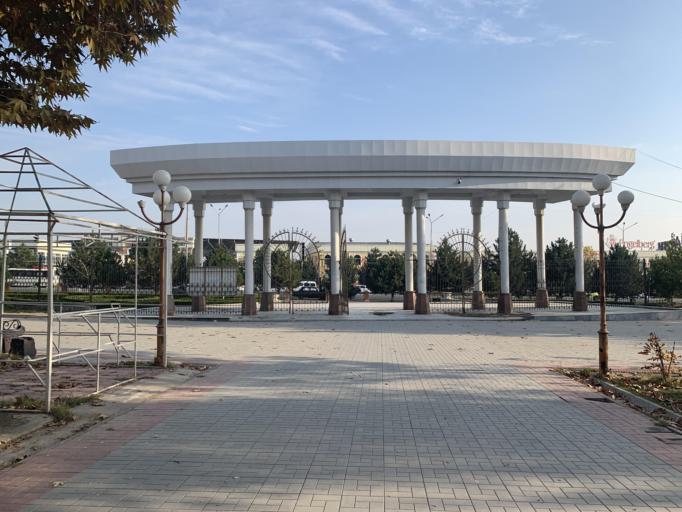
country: UZ
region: Namangan
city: Namangan Shahri
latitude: 40.9986
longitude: 71.5970
